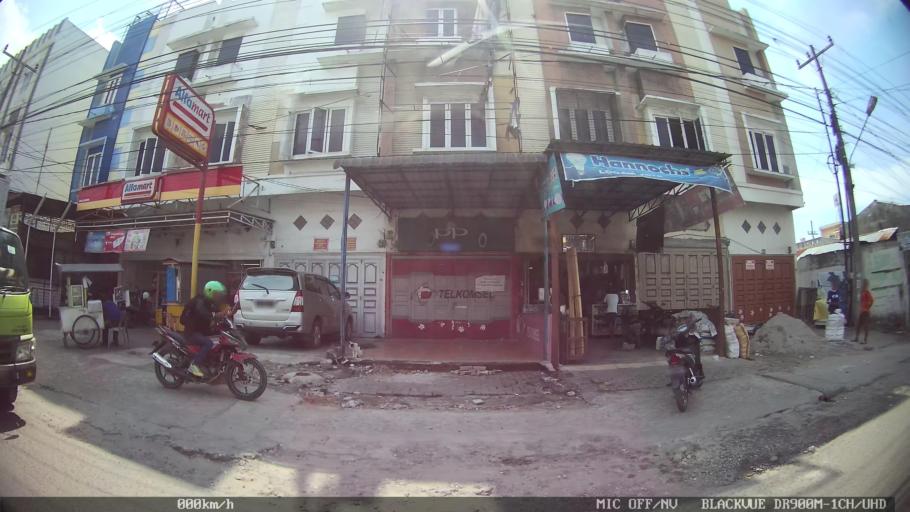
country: ID
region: North Sumatra
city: Medan
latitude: 3.6207
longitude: 98.6651
